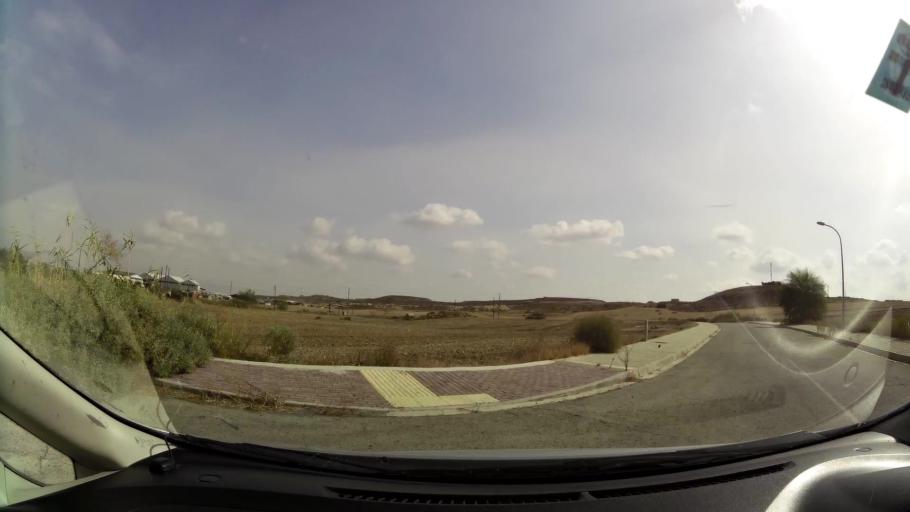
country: CY
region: Lefkosia
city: Geri
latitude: 35.0686
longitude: 33.4026
